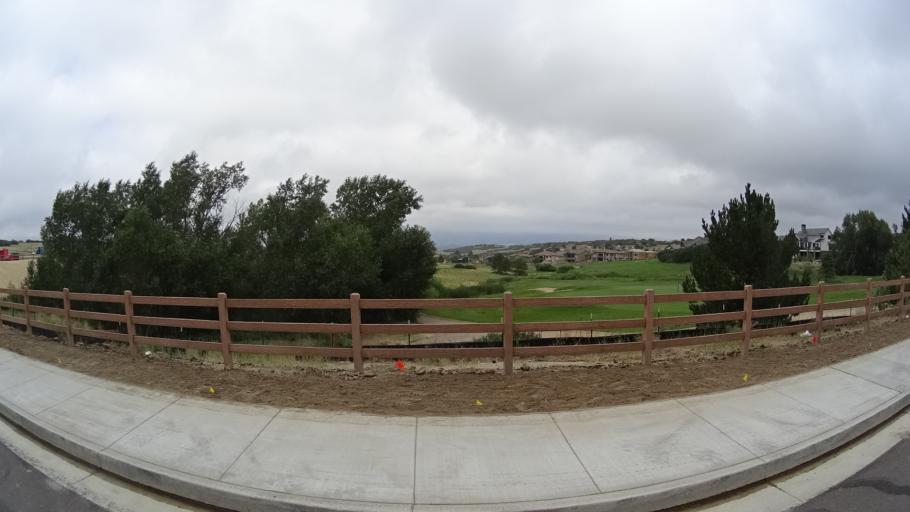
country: US
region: Colorado
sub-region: El Paso County
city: Gleneagle
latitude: 39.0257
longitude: -104.7931
